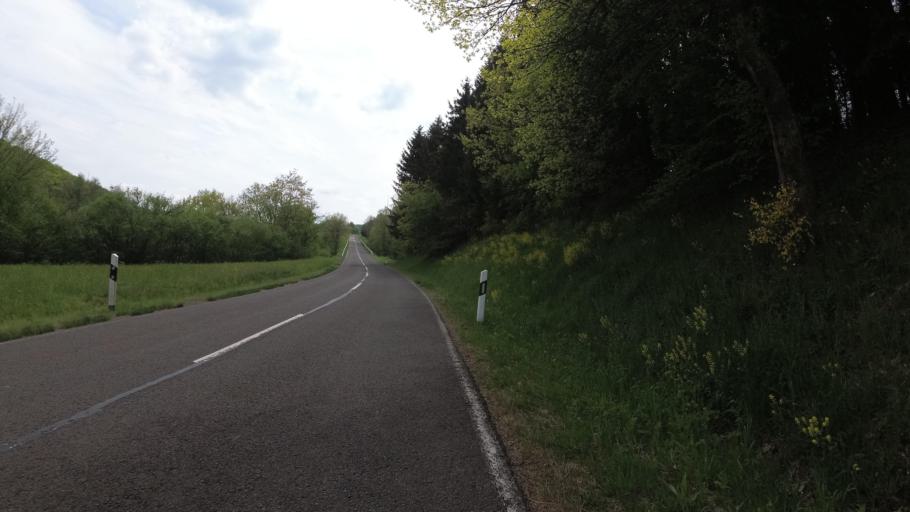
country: DE
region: Rheinland-Pfalz
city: Eckersweiler
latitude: 49.5670
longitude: 7.2894
